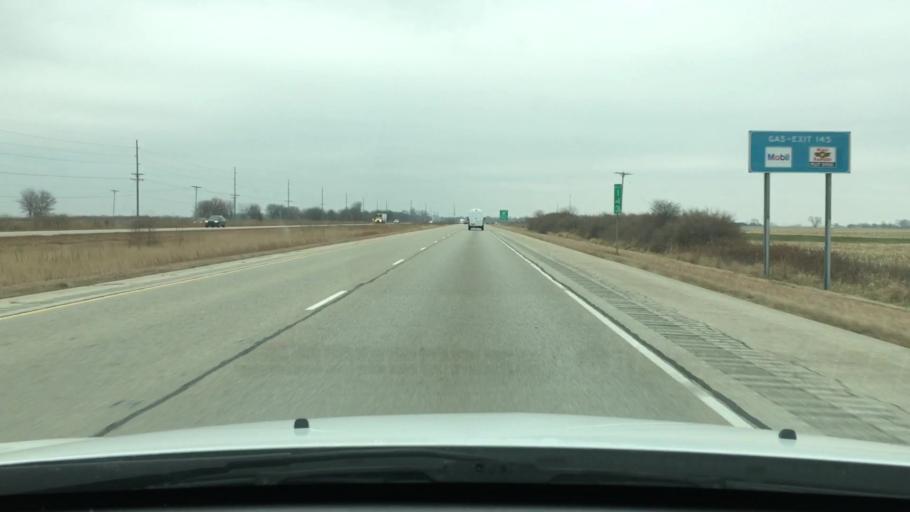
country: US
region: Illinois
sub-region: Logan County
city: Atlanta
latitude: 40.2971
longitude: -89.1886
